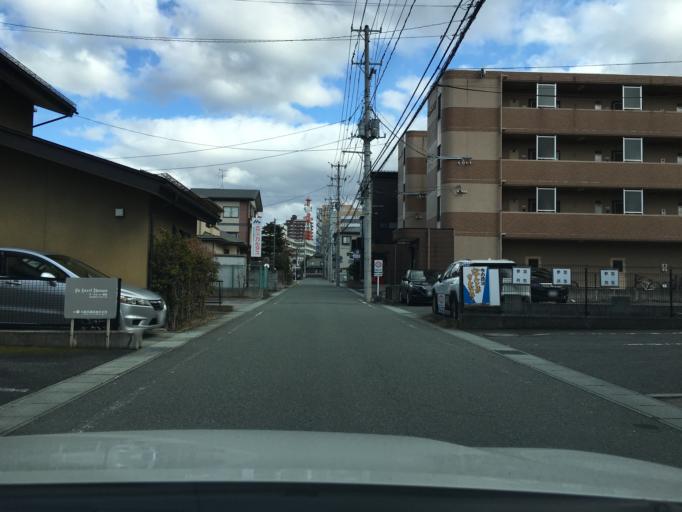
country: JP
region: Yamagata
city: Yamagata-shi
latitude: 38.2524
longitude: 140.3271
